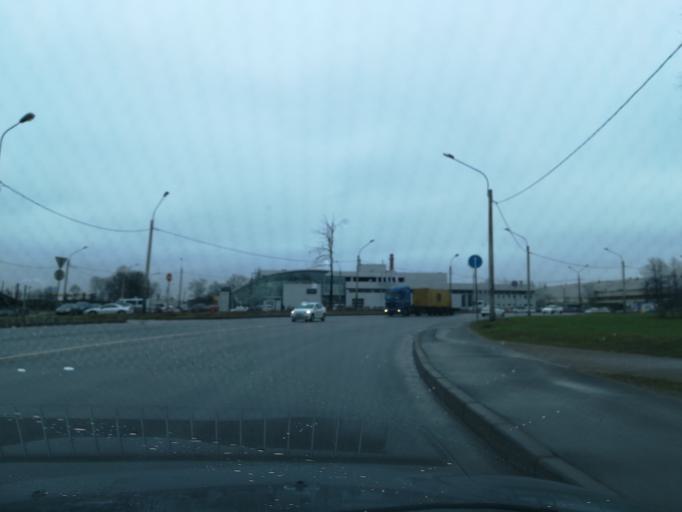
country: RU
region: St.-Petersburg
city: Avtovo
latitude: 59.8622
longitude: 30.2610
